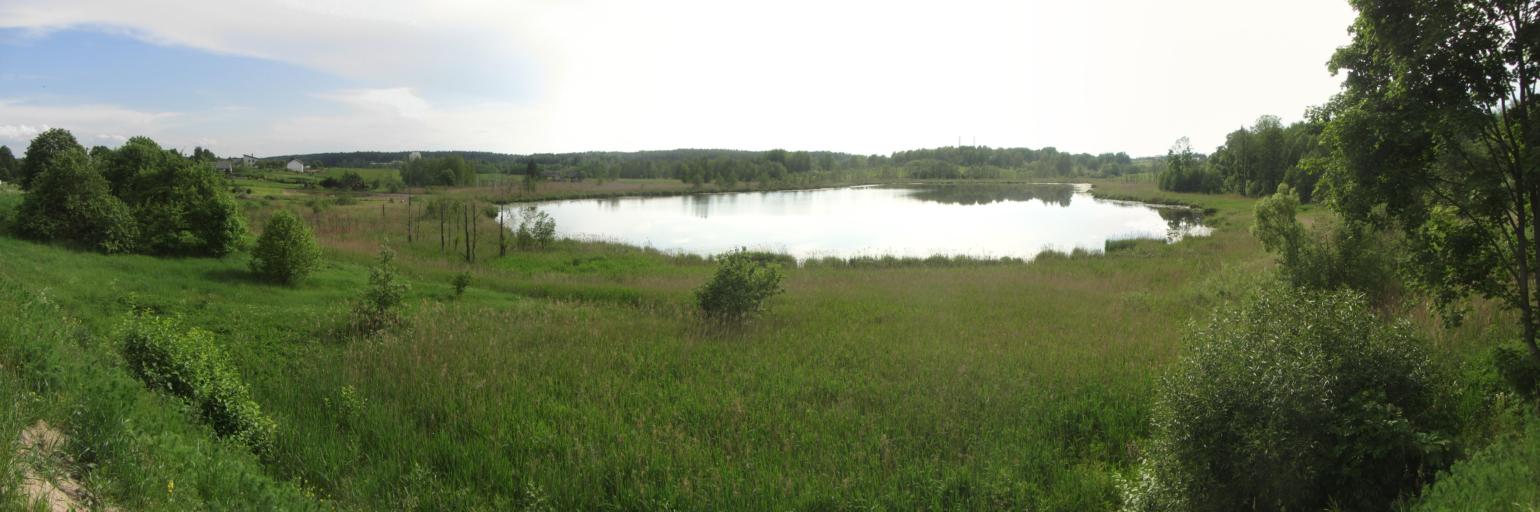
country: LT
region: Vilnius County
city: Elektrenai
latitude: 54.7772
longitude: 24.7178
